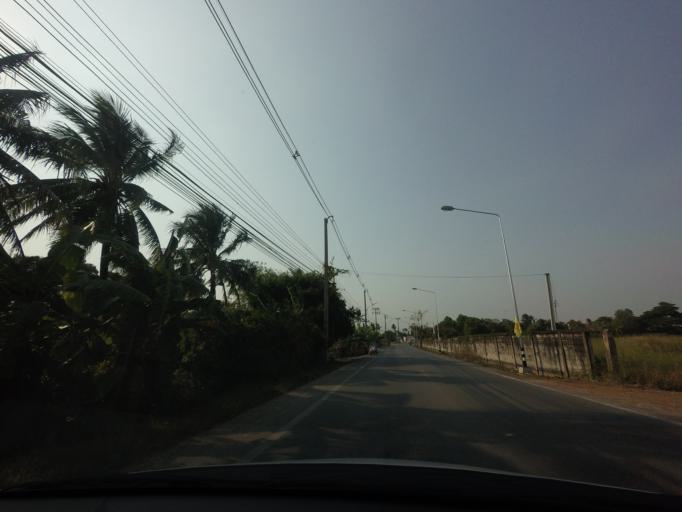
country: TH
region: Nakhon Pathom
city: Sam Phran
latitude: 13.6974
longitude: 100.2078
